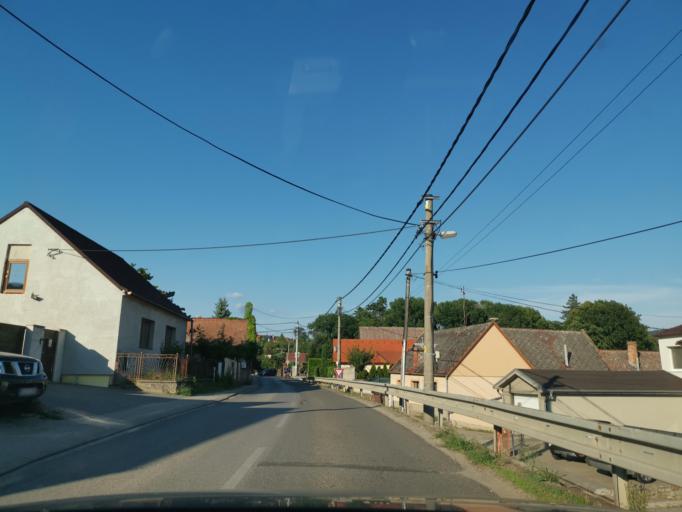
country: SK
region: Bratislavsky
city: Stupava
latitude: 48.2775
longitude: 17.0370
